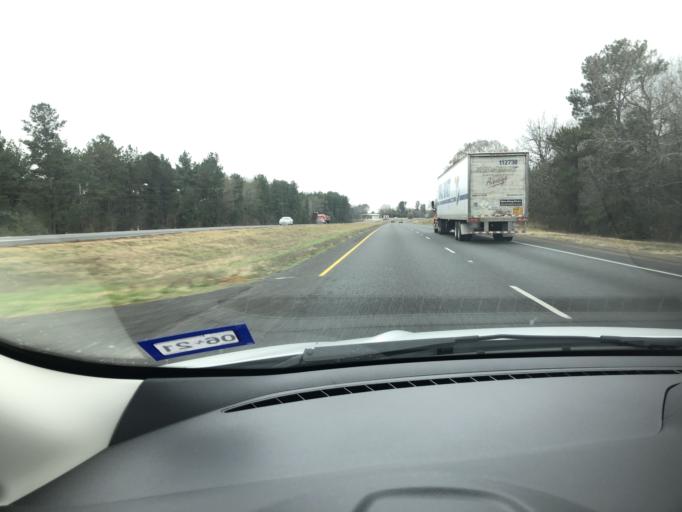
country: US
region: Texas
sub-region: Nacogdoches County
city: Nacogdoches
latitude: 31.5116
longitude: -94.7006
